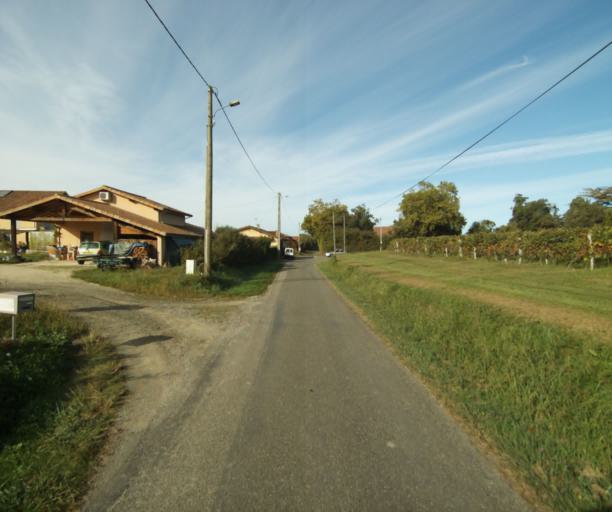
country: FR
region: Midi-Pyrenees
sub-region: Departement du Gers
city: Eauze
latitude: 43.8867
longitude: 0.1332
